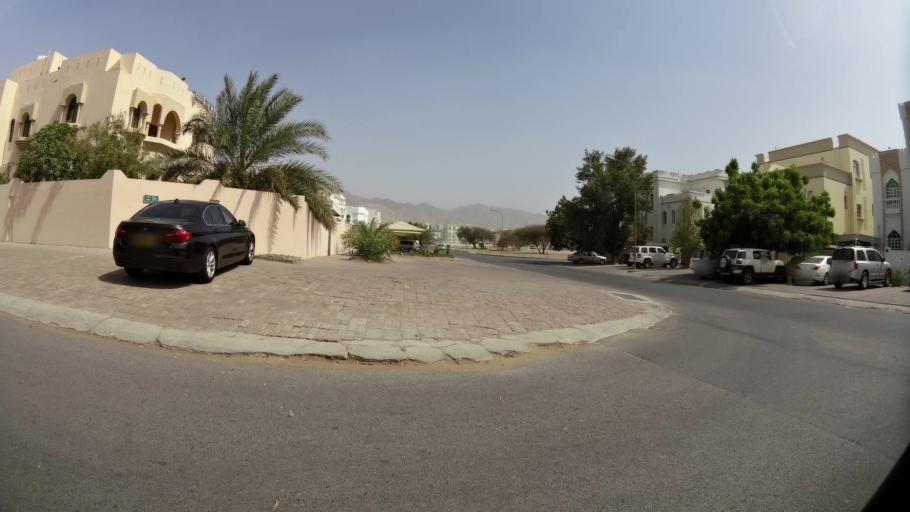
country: OM
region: Muhafazat Masqat
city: Bawshar
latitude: 23.5795
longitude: 58.4026
